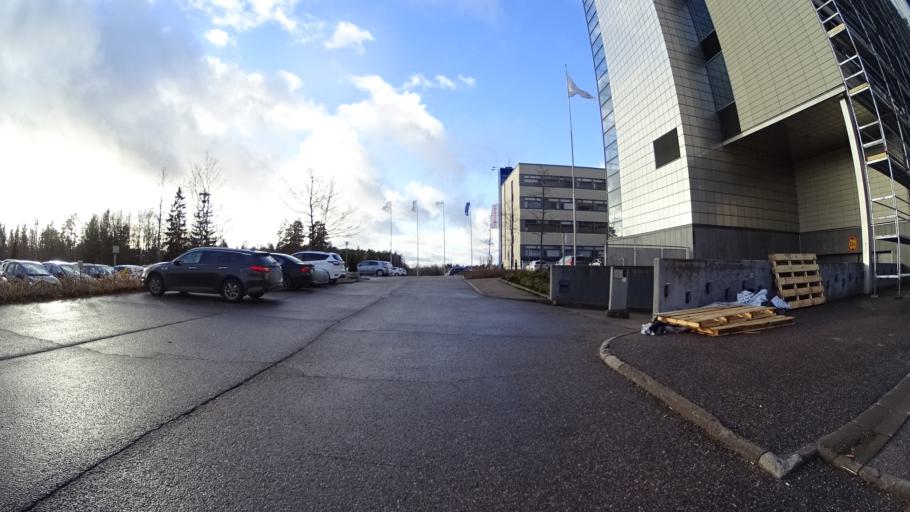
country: FI
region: Uusimaa
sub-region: Helsinki
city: Kilo
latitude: 60.2045
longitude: 24.7566
